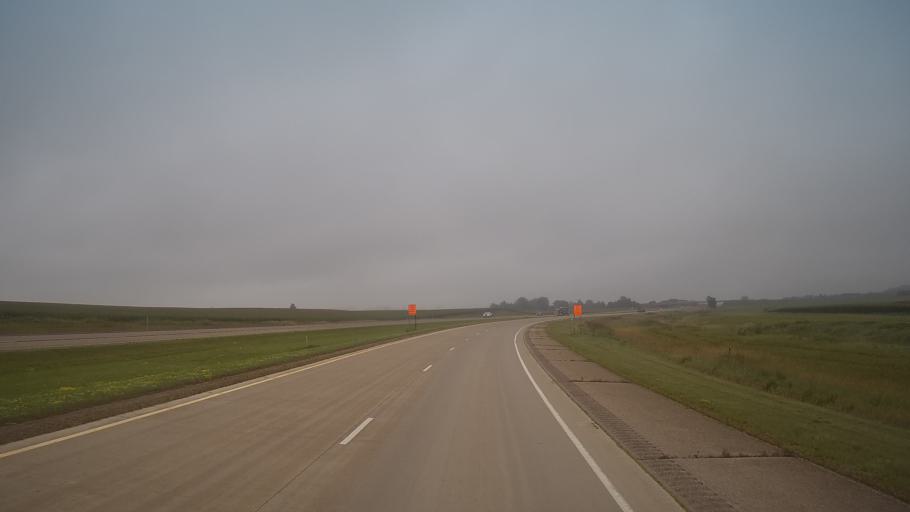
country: US
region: Minnesota
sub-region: Freeborn County
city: Albert Lea
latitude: 43.6788
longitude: -93.4807
